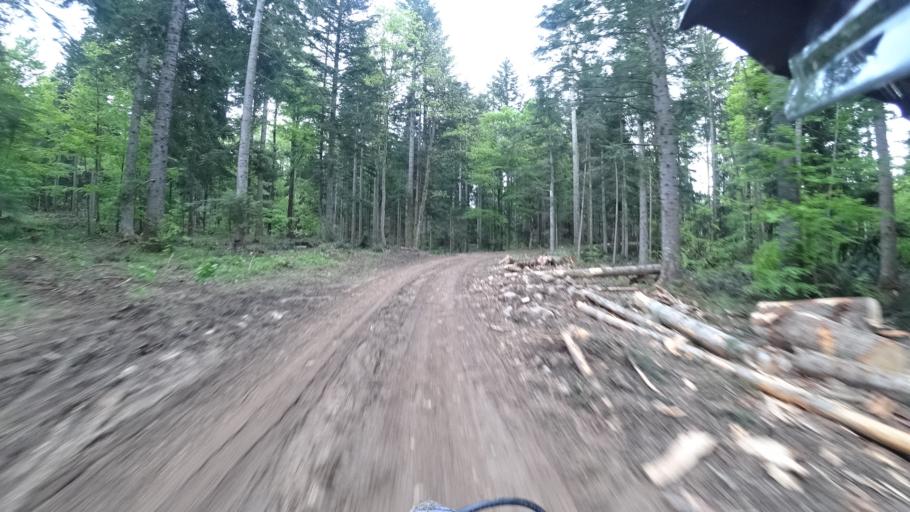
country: HR
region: Karlovacka
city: Plaski
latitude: 44.9492
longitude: 15.4152
